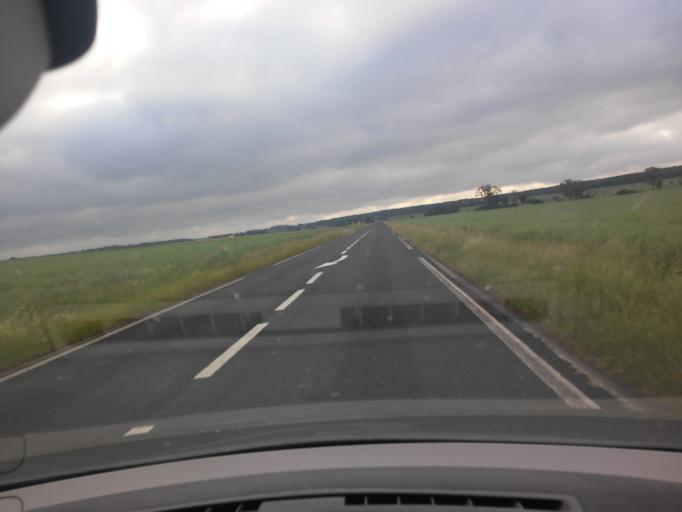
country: FR
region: Lorraine
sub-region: Departement de la Meuse
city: Vigneulles-les-Hattonchatel
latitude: 48.9865
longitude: 5.7870
